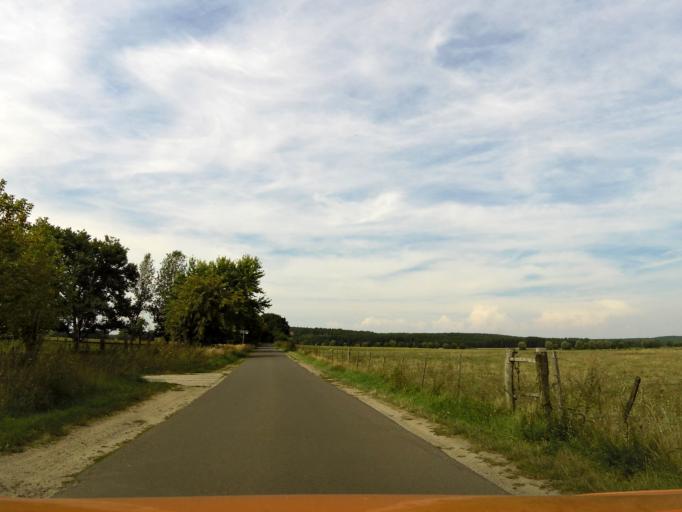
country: DE
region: Brandenburg
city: Michendorf
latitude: 52.2360
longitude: 13.1081
